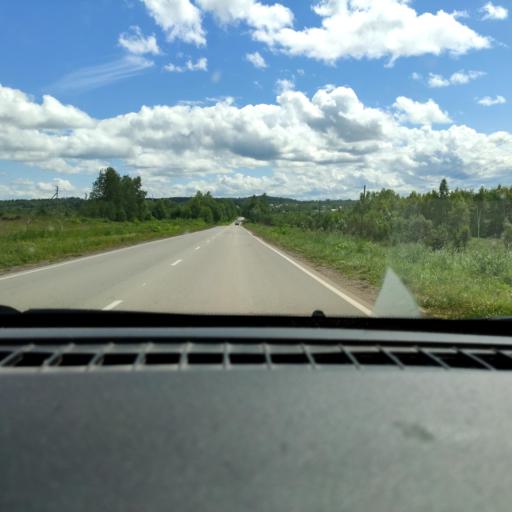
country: RU
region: Perm
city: Overyata
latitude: 58.1207
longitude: 55.8191
